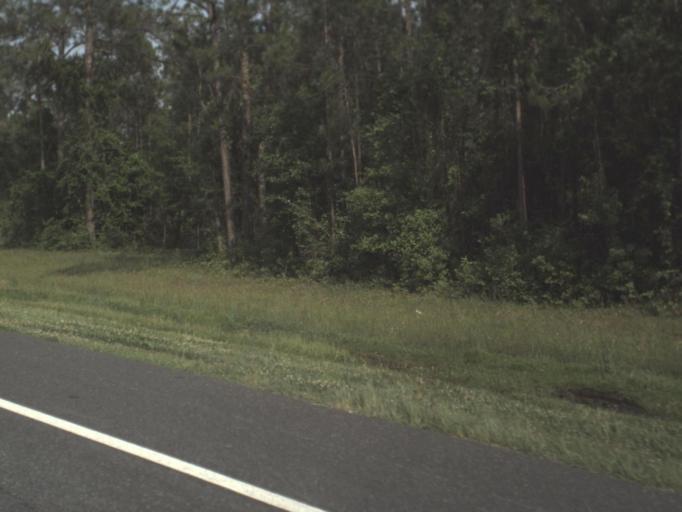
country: US
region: Florida
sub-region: Baker County
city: Macclenny
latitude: 30.2652
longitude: -82.0987
